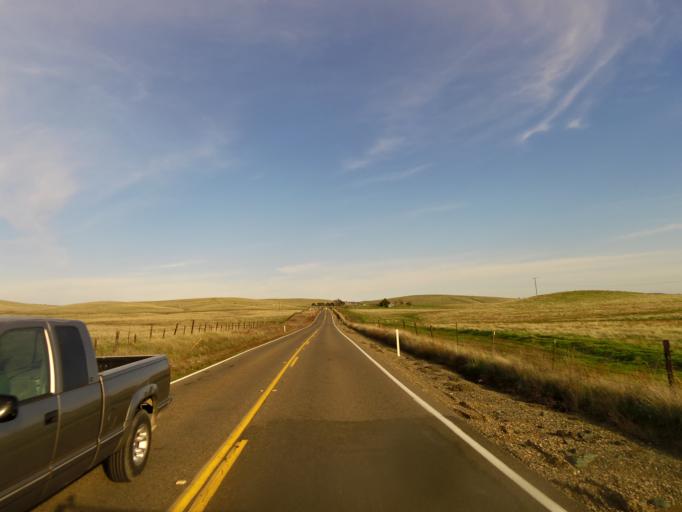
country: US
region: California
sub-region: El Dorado County
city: El Dorado Hills
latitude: 38.6251
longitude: -121.1001
